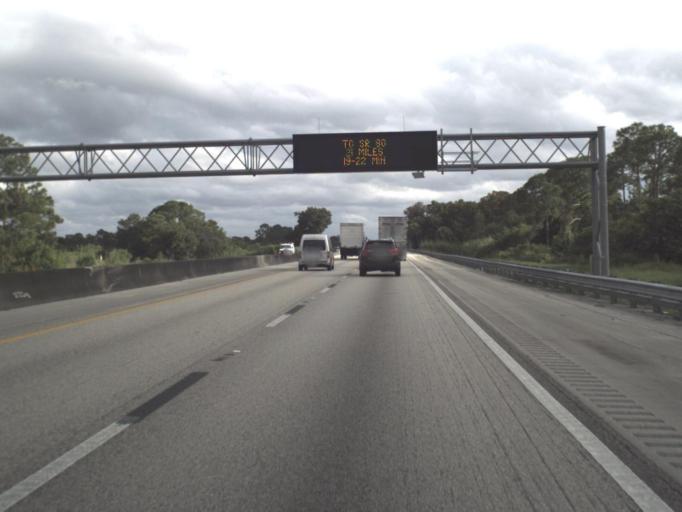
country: US
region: Florida
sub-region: Palm Beach County
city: Limestone Creek
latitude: 26.9744
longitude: -80.1802
